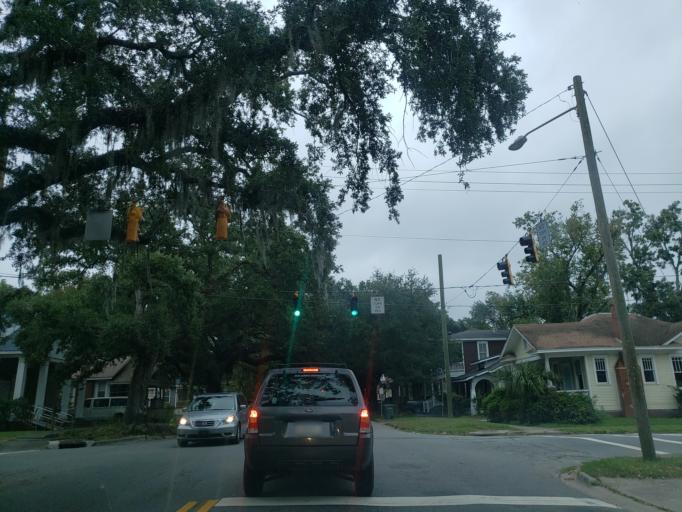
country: US
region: Georgia
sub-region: Chatham County
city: Savannah
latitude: 32.0538
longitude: -81.0878
